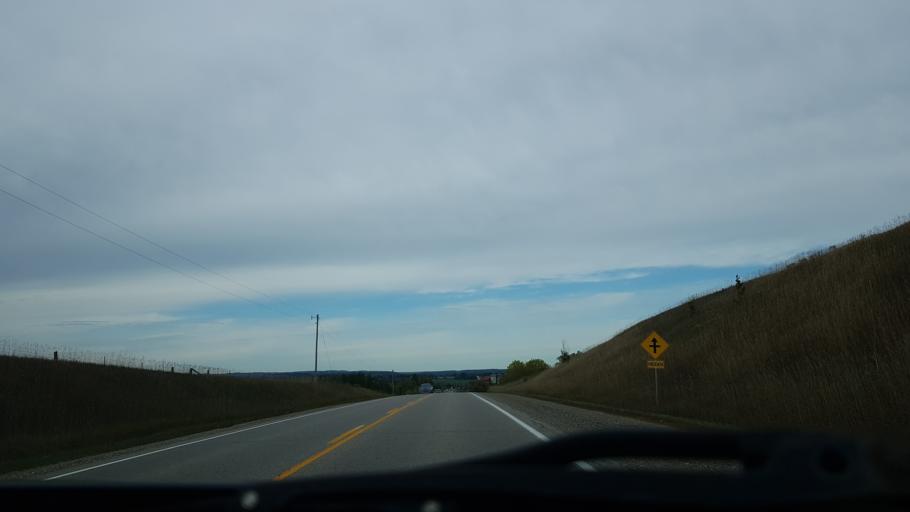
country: CA
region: Ontario
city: Shelburne
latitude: 44.1043
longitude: -80.0243
